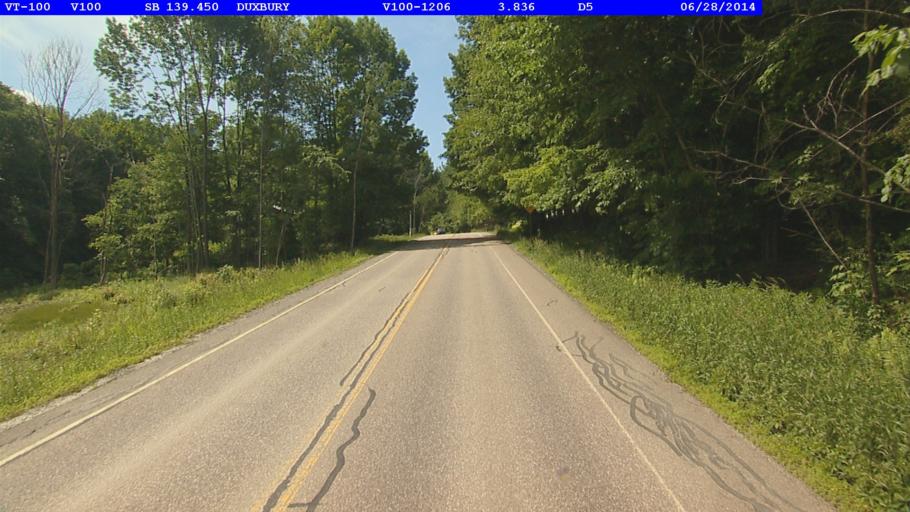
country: US
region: Vermont
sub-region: Washington County
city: Waterbury
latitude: 44.2995
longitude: -72.7735
